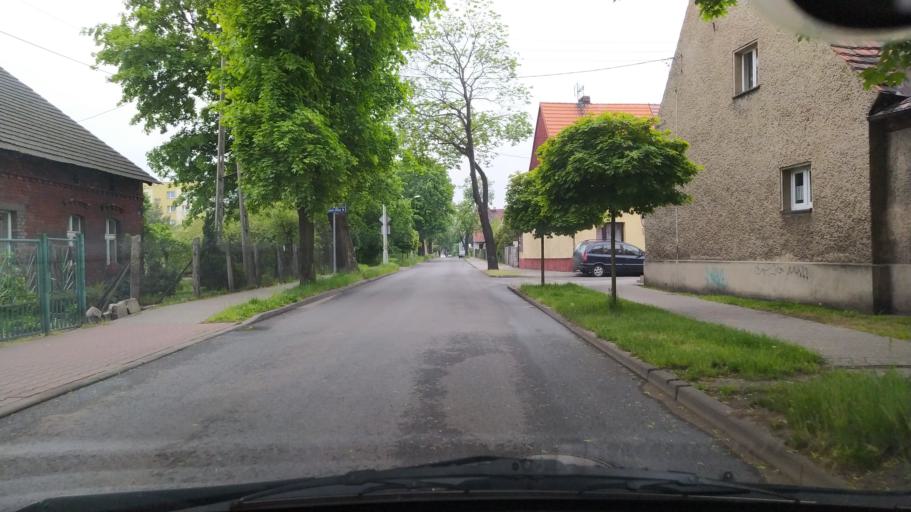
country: PL
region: Silesian Voivodeship
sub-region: Powiat gliwicki
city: Przyszowice
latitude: 50.2929
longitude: 18.7399
